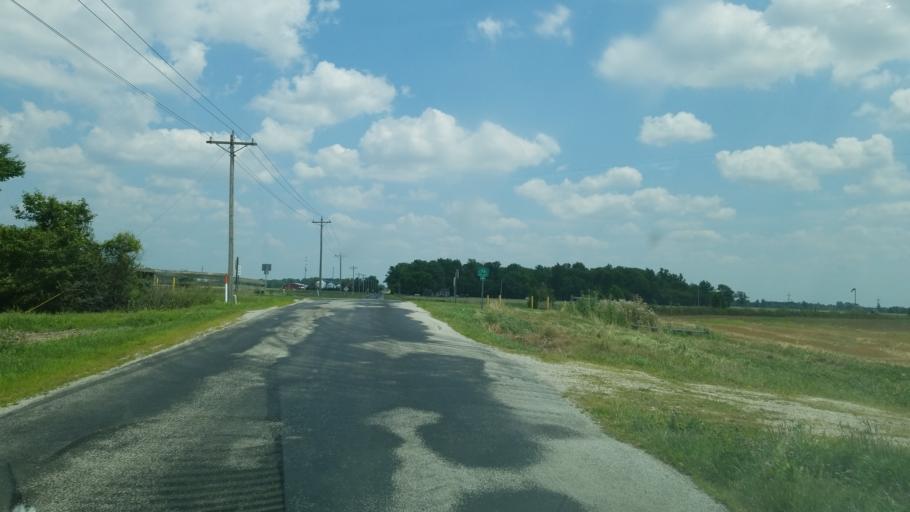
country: US
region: Ohio
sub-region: Wood County
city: North Baltimore
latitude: 41.2409
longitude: -83.6746
